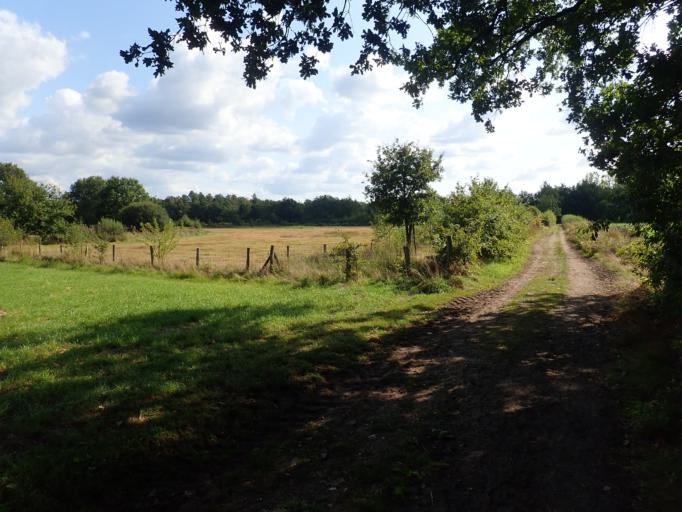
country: BE
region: Flanders
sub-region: Provincie Antwerpen
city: Lille
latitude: 51.2882
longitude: 4.8171
